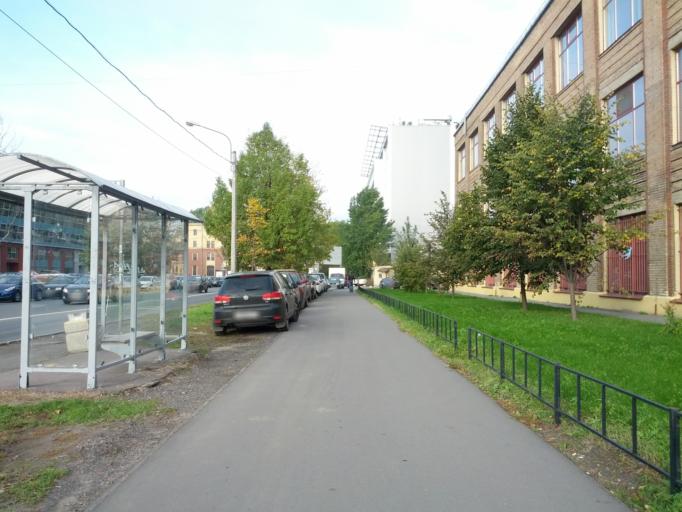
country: RU
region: Leningrad
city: Svetlanovskiy
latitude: 59.9863
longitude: 30.3240
